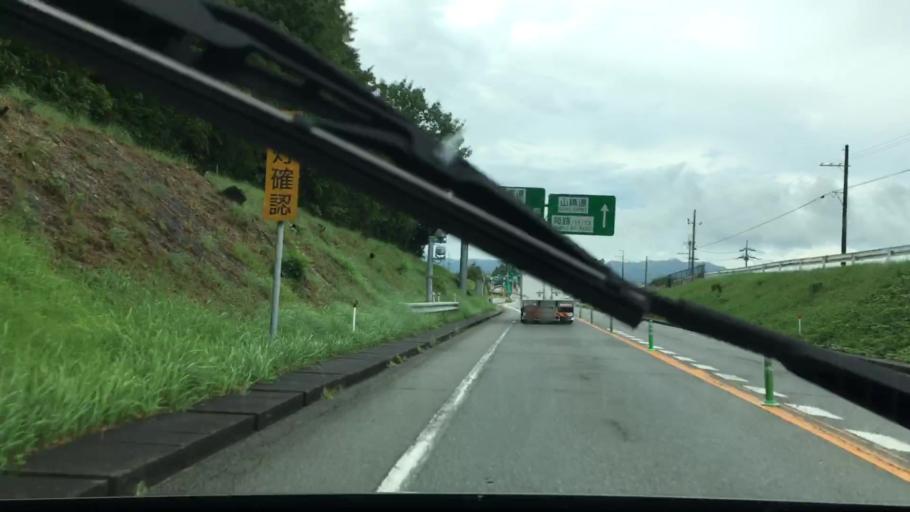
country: JP
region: Hyogo
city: Himeji
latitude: 34.9602
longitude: 134.7698
